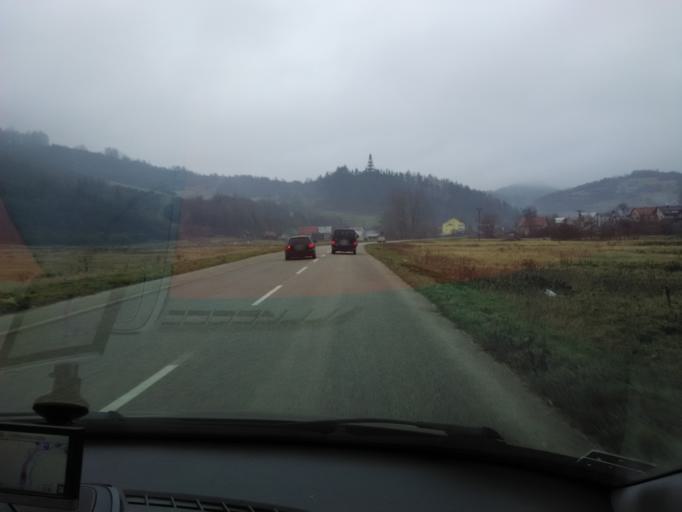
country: SK
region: Zilinsky
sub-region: Okres Zilina
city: Terchova
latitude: 49.2565
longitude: 19.0188
